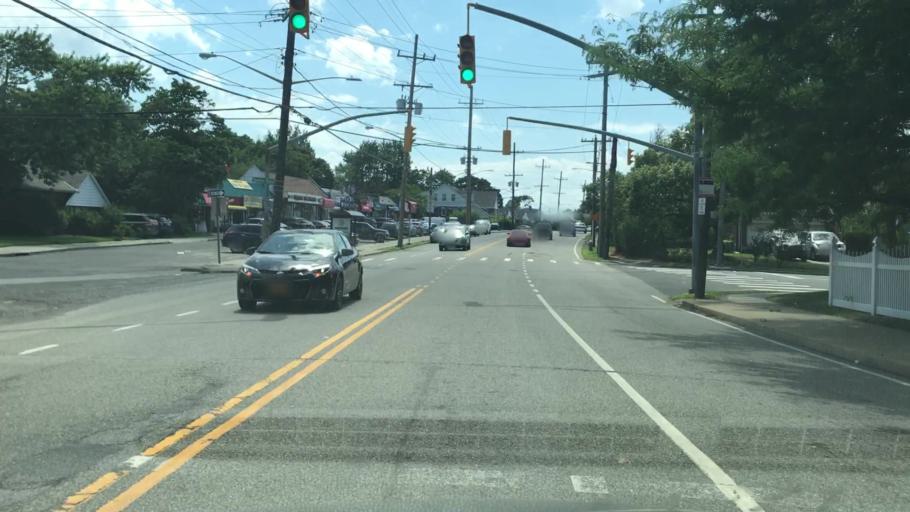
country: US
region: New York
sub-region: Nassau County
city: North Valley Stream
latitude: 40.6822
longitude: -73.7128
